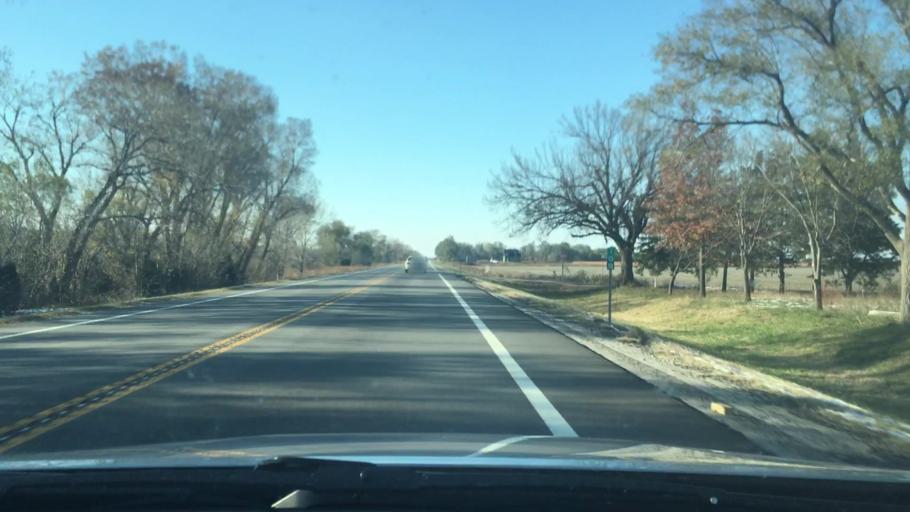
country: US
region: Kansas
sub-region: Reno County
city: Nickerson
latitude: 38.1074
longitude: -98.0252
